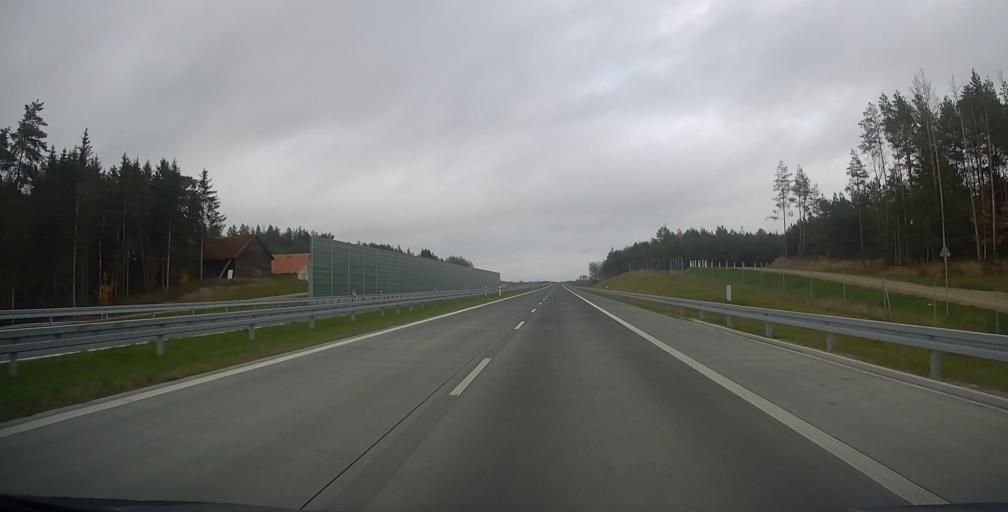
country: PL
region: Podlasie
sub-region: Powiat grajewski
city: Rajgrod
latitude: 53.8710
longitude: 22.6375
